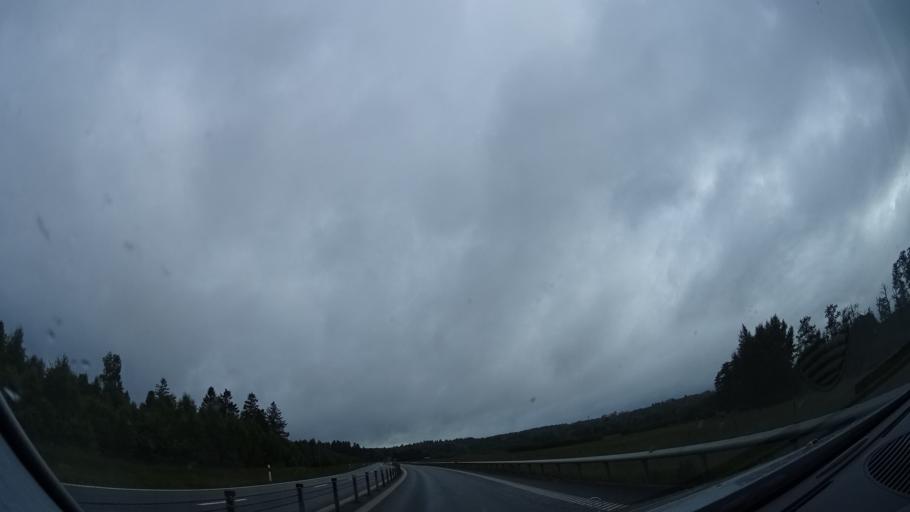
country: SE
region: Skane
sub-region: Hoors Kommun
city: Satofta
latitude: 55.8953
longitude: 13.5239
